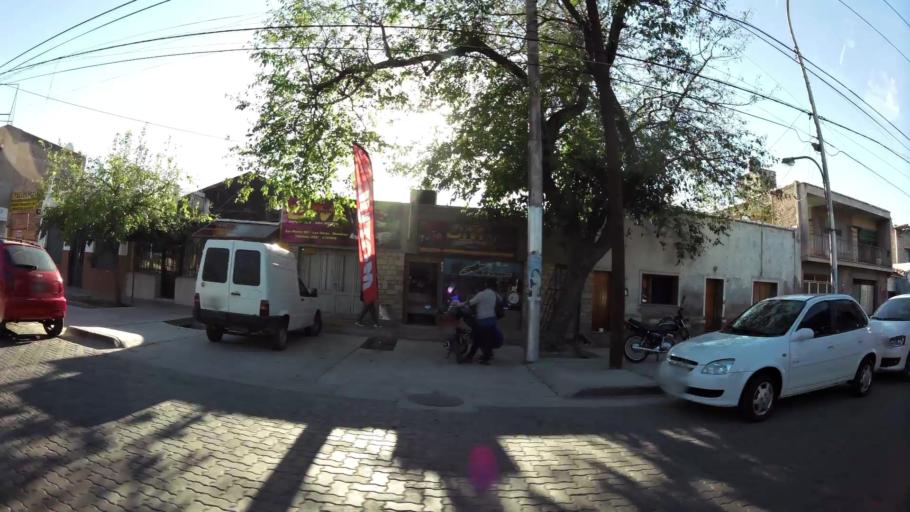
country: AR
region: Mendoza
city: Las Heras
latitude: -32.8572
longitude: -68.8334
